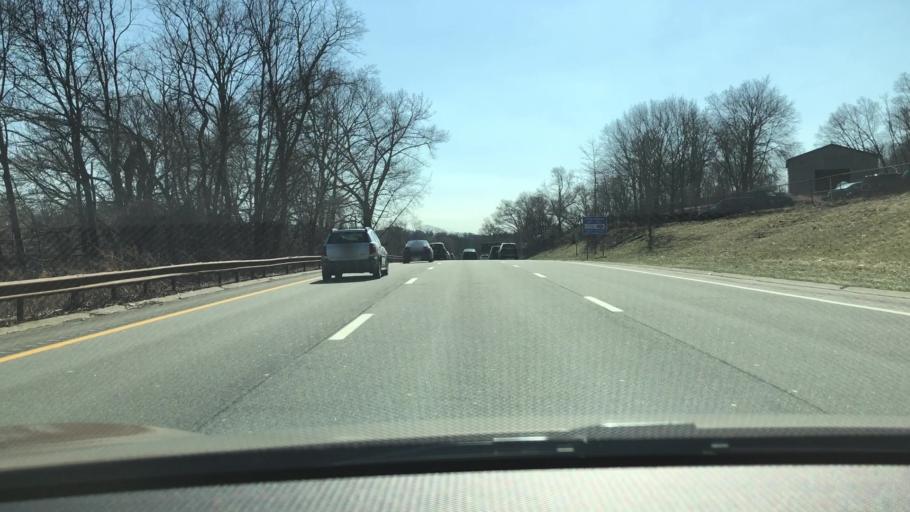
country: US
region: New York
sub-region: Westchester County
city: Tuckahoe
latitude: 40.9620
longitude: -73.8528
